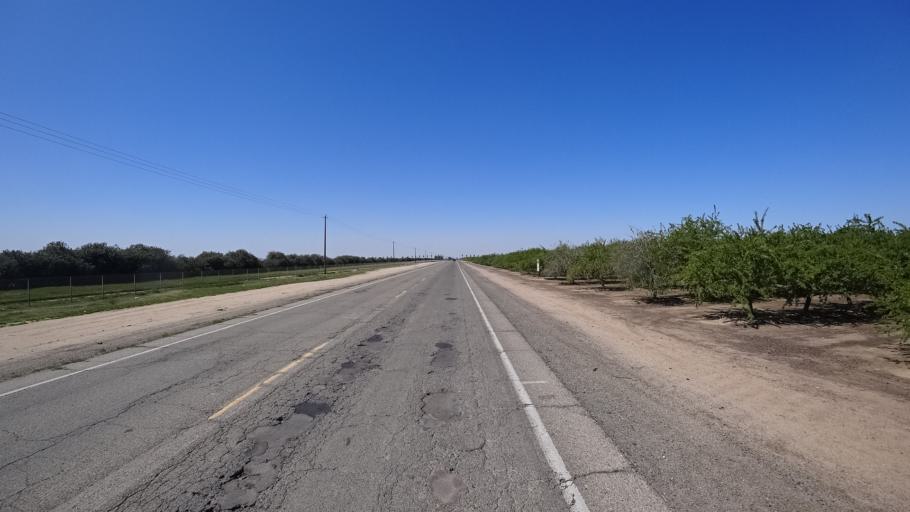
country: US
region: California
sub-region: Fresno County
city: West Park
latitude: 36.7063
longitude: -119.9183
